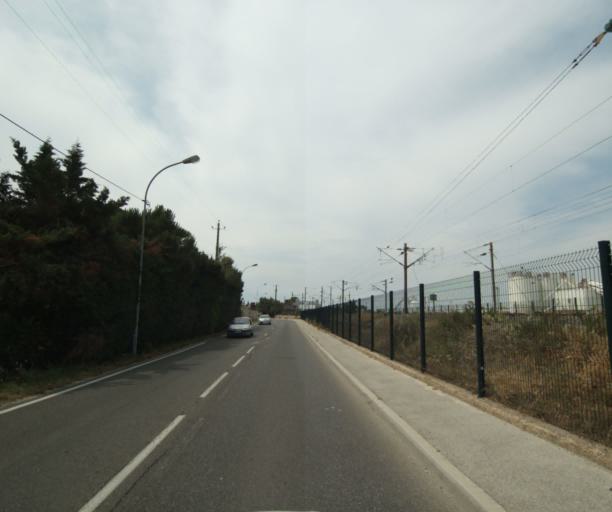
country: FR
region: Provence-Alpes-Cote d'Azur
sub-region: Departement du Var
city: La Farlede
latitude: 43.1388
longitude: 6.0376
